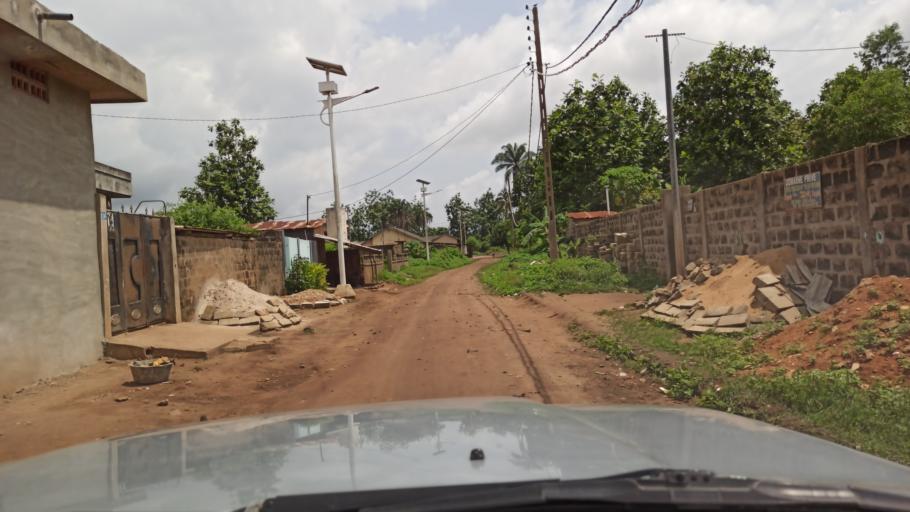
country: BJ
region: Queme
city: Porto-Novo
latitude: 6.4670
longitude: 2.6326
